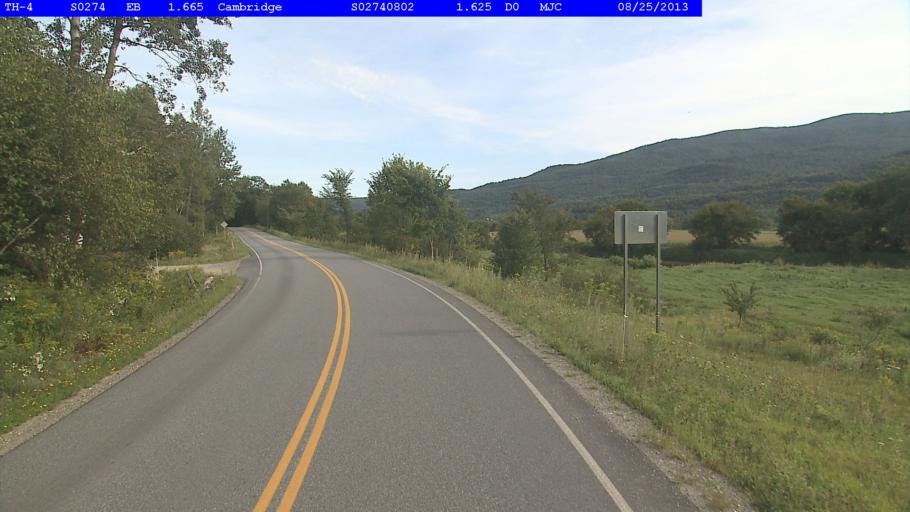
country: US
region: Vermont
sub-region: Lamoille County
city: Johnson
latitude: 44.6621
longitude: -72.7587
